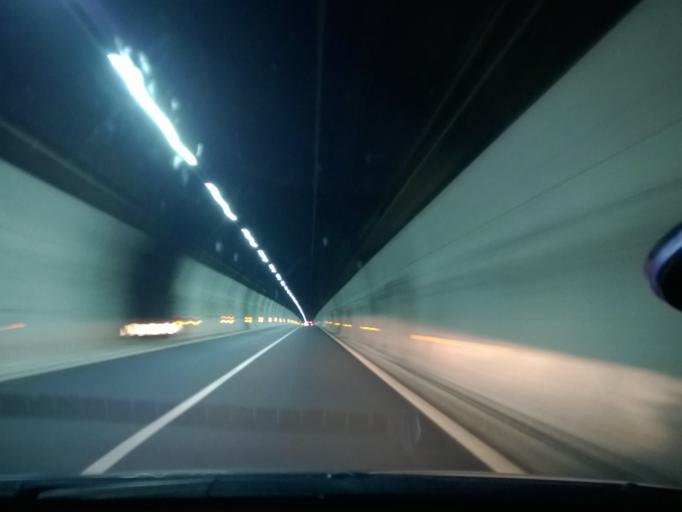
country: IT
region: Veneto
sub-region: Provincia di Treviso
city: Revine
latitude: 46.0008
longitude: 12.2741
